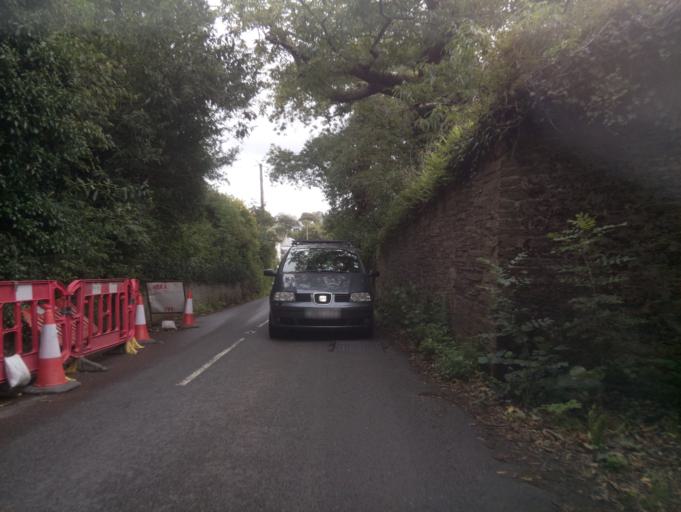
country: GB
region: England
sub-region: Devon
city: Salcombe
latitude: 50.2737
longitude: -3.6766
